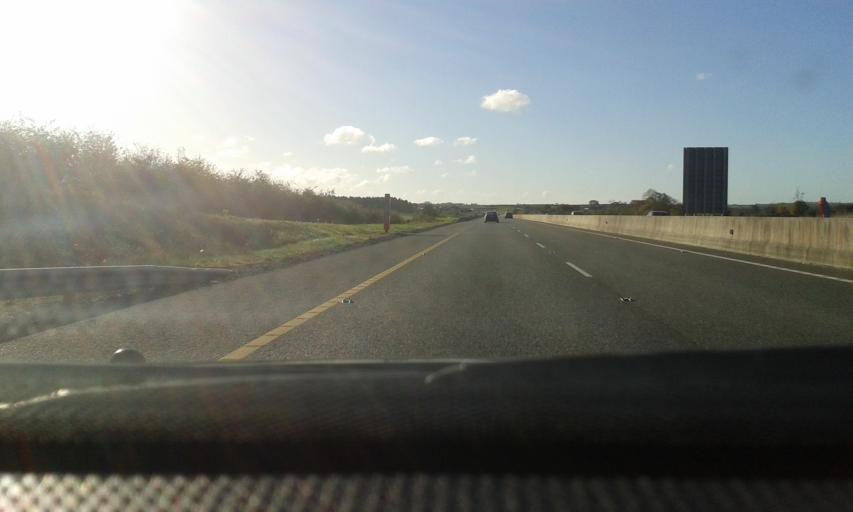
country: IE
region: Leinster
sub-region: Laois
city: Rathdowney
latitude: 52.8520
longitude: -7.4906
